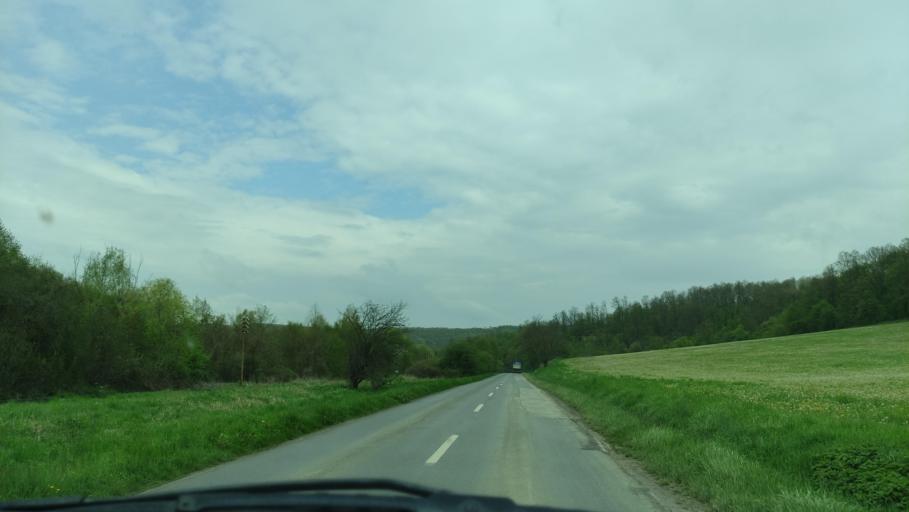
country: HU
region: Baranya
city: Komlo
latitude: 46.2209
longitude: 18.2410
